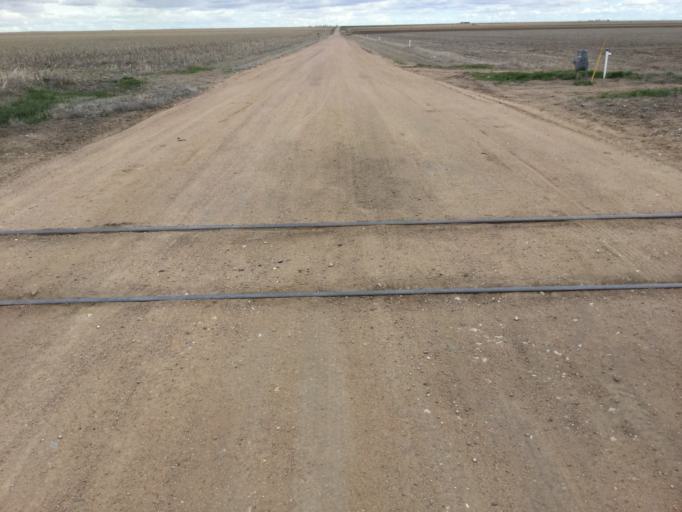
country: US
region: Kansas
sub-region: Sherman County
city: Goodland
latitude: 39.3405
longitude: -101.7636
